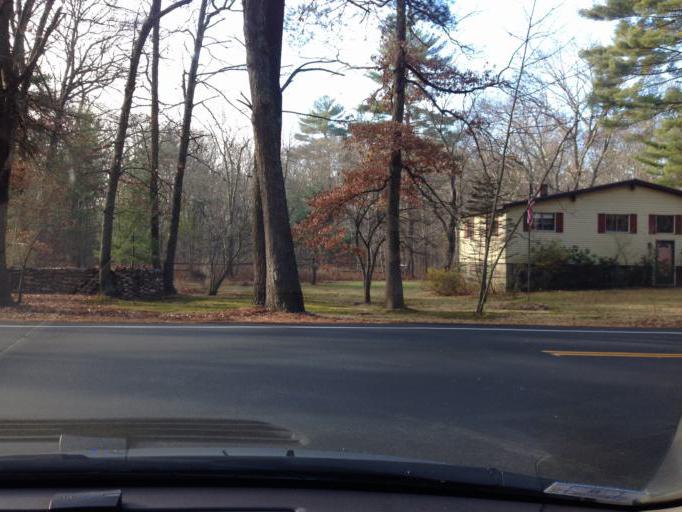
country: US
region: Massachusetts
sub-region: Middlesex County
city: Bedford
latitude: 42.5051
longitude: -71.3021
